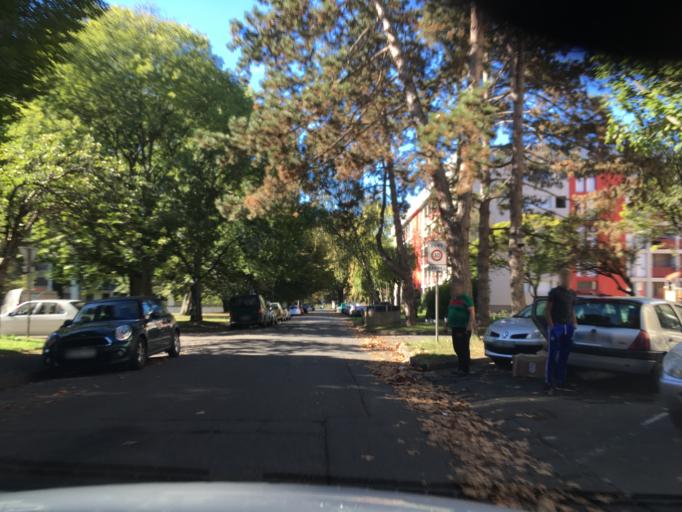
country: FR
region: Aquitaine
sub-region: Departement des Pyrenees-Atlantiques
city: Pau
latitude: 43.3090
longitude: -0.3669
